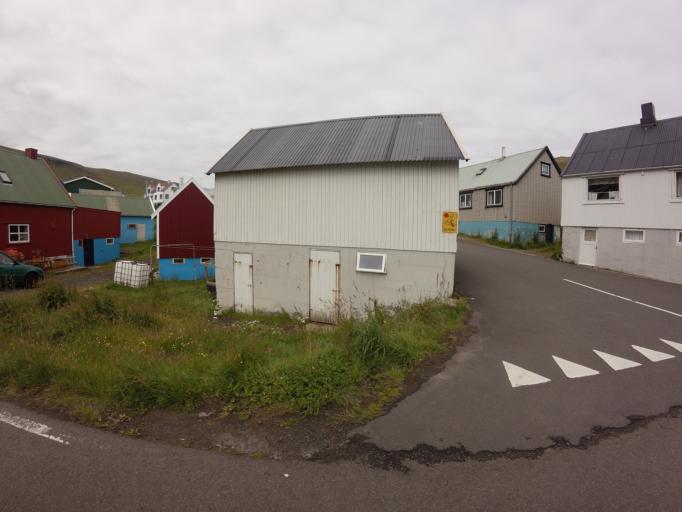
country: FO
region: Suduroy
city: Tvoroyri
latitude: 61.6319
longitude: -6.9289
